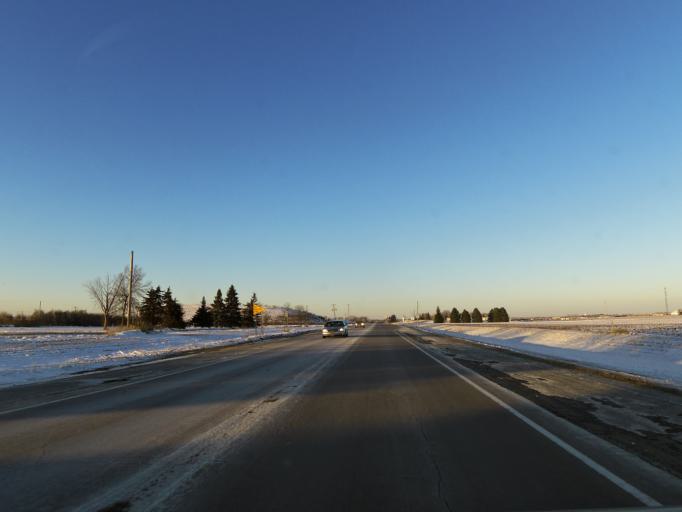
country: US
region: Minnesota
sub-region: Dakota County
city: Rosemount
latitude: 44.7008
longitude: -93.1365
